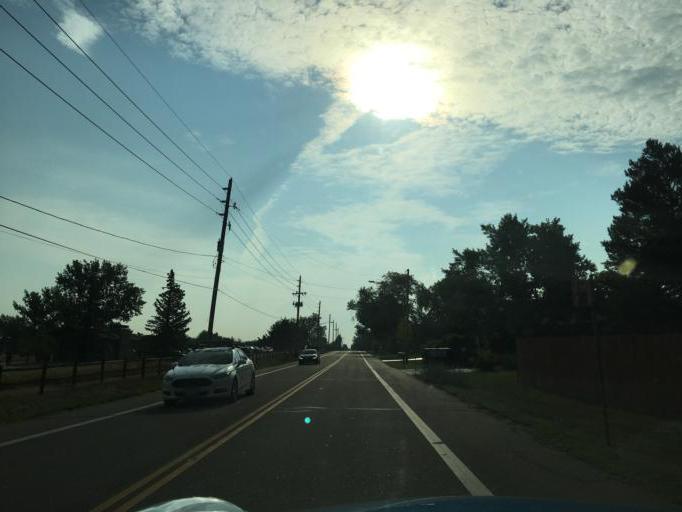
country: US
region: Colorado
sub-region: Jefferson County
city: Wheat Ridge
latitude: 39.7547
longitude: -105.1039
